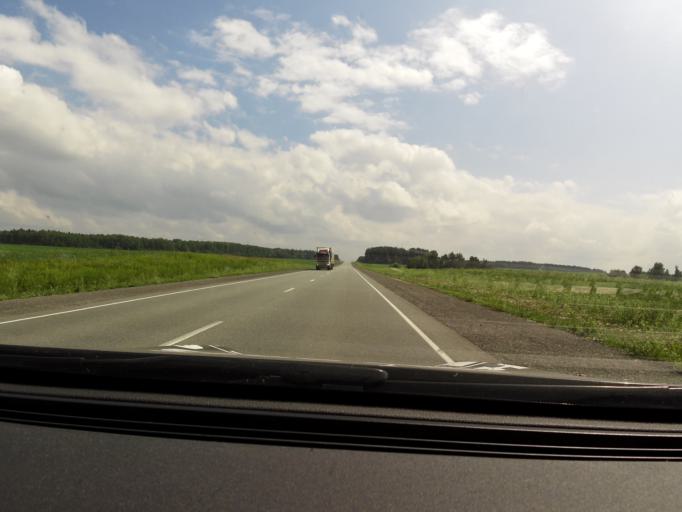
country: RU
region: Perm
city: Suksun
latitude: 57.0297
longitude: 57.4520
